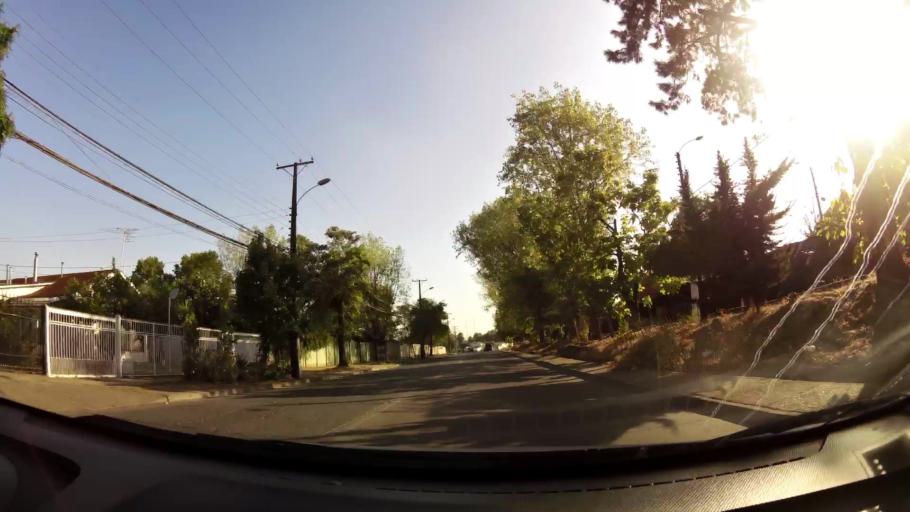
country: CL
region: Maule
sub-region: Provincia de Talca
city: Talca
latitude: -35.4069
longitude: -71.6548
